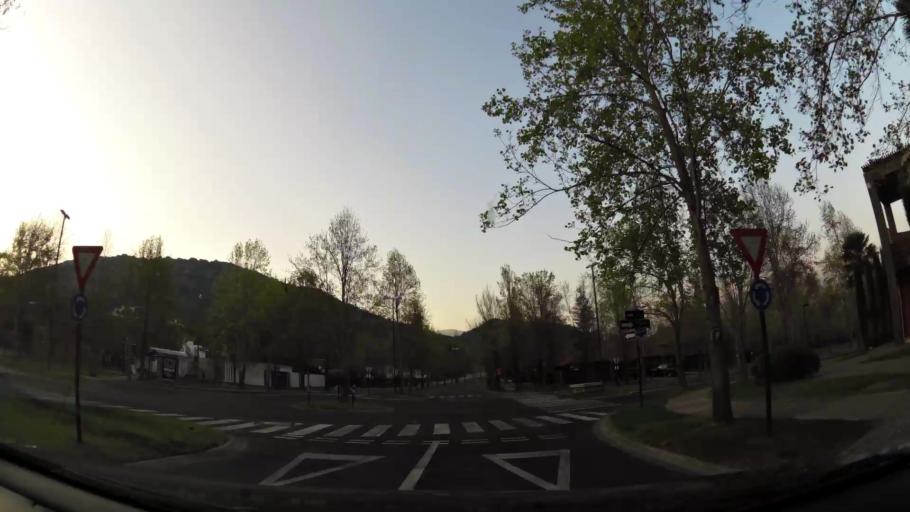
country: CL
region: Santiago Metropolitan
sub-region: Provincia de Chacabuco
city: Chicureo Abajo
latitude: -33.3385
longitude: -70.5539
